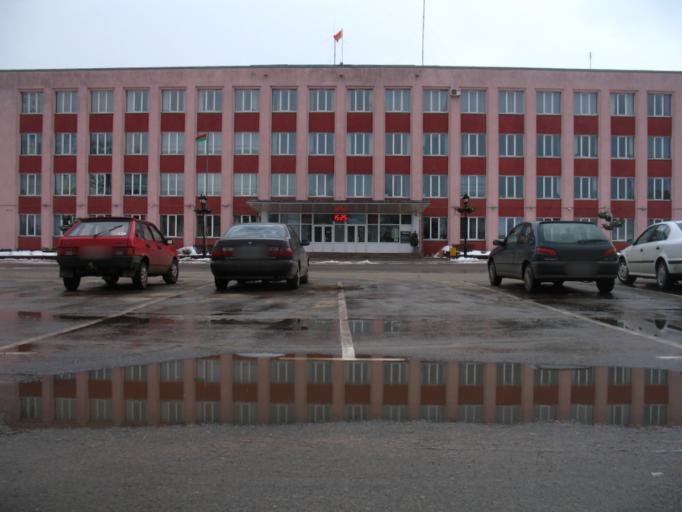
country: BY
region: Vitebsk
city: Pastavy
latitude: 55.1131
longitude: 26.8397
